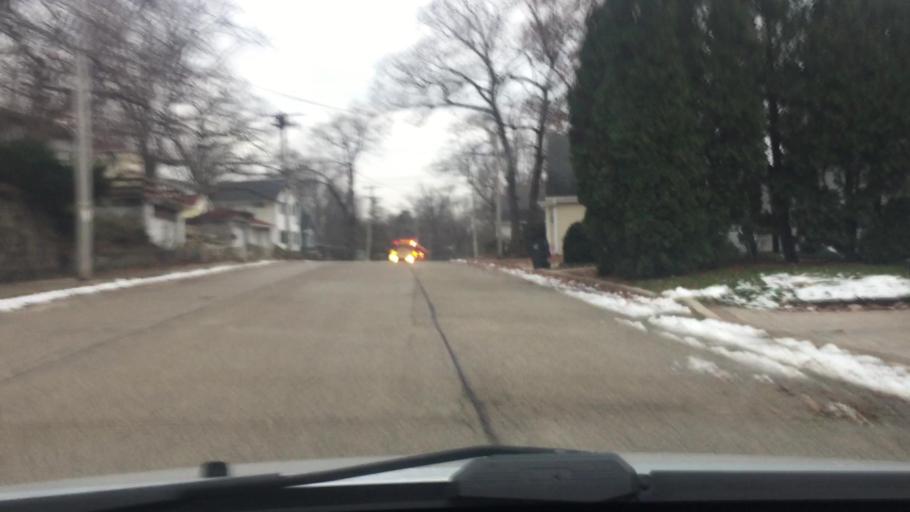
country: US
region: Wisconsin
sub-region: Waukesha County
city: Pewaukee
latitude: 43.0773
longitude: -88.2689
